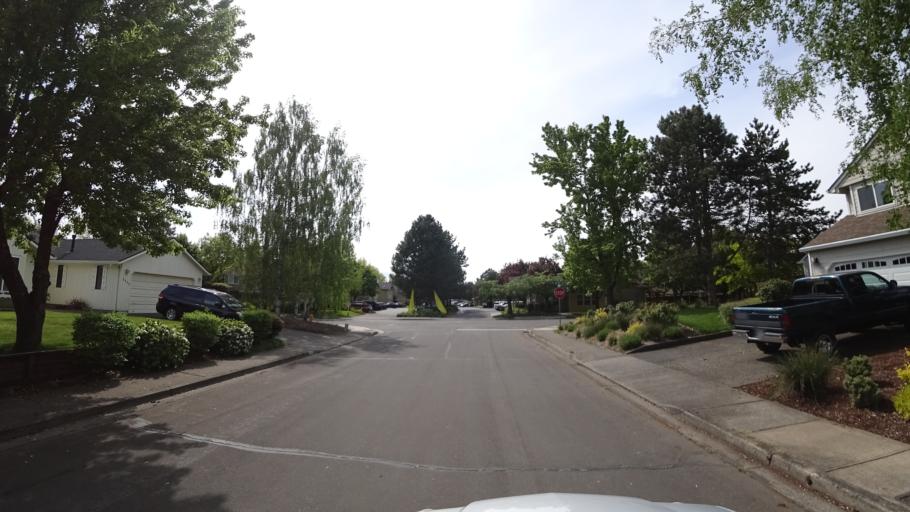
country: US
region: Oregon
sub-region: Washington County
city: Rockcreek
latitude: 45.5343
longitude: -122.9287
